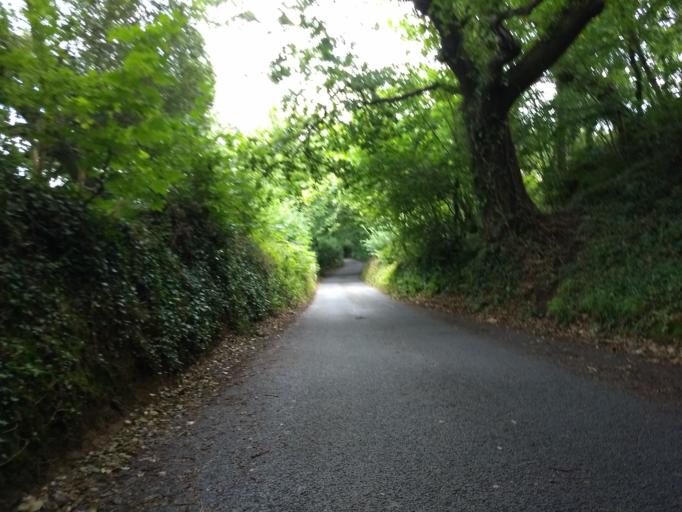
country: GB
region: England
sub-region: Isle of Wight
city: Newport
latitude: 50.6743
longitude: -1.2949
